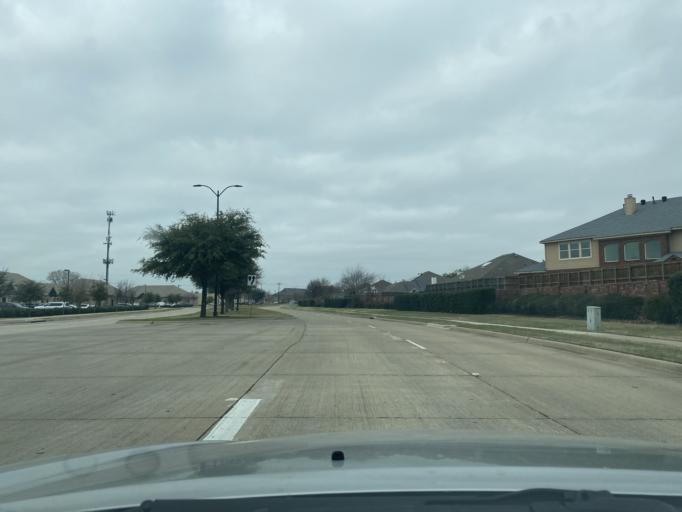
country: US
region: Texas
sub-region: Collin County
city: Frisco
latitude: 33.1134
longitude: -96.8011
